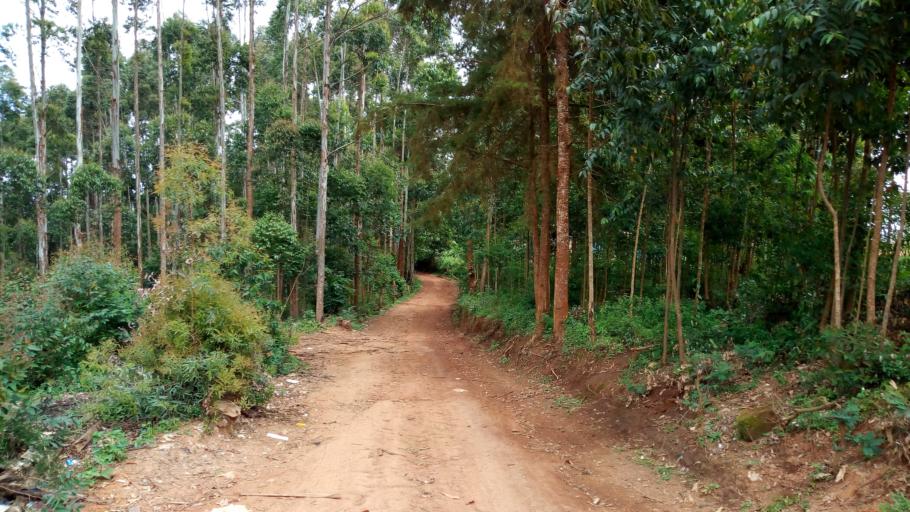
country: KE
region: Makueni
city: Wote
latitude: -1.6560
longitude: 37.4560
